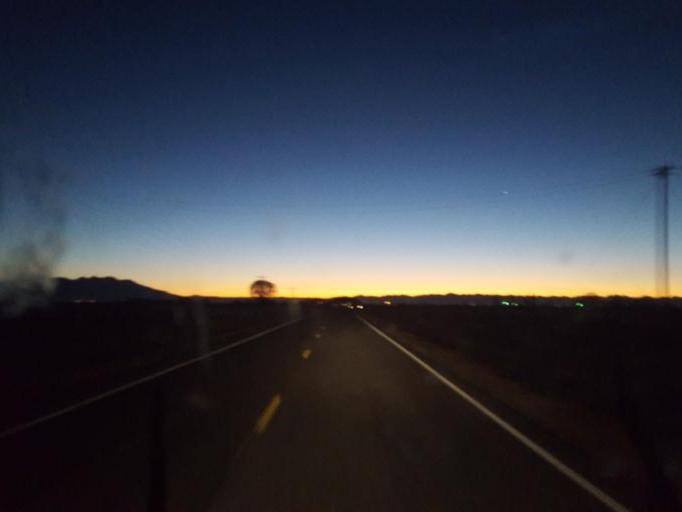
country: US
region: Colorado
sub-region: Rio Grande County
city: Monte Vista
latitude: 37.4300
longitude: -106.0486
